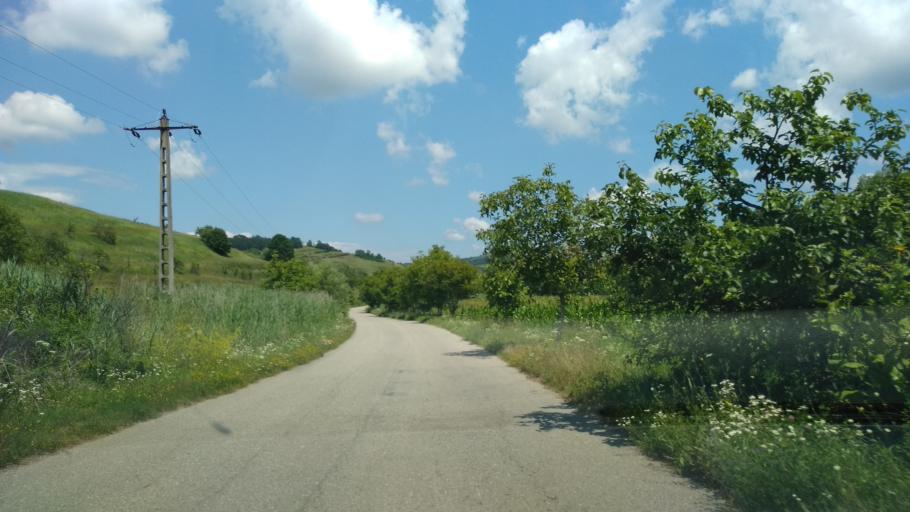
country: RO
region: Hunedoara
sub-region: Comuna Bosorod
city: Bosorod
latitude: 45.7047
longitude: 23.1040
